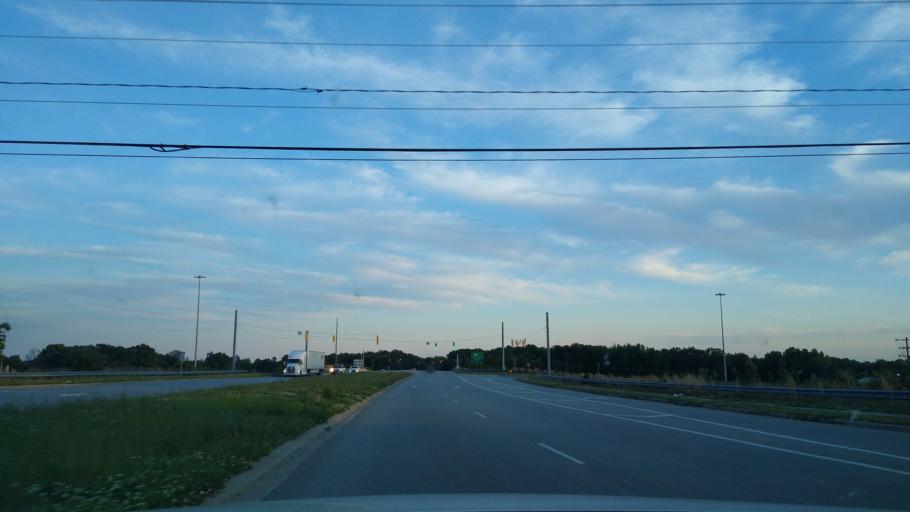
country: US
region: North Carolina
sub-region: Forsyth County
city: Kernersville
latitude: 36.1087
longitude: -80.0459
